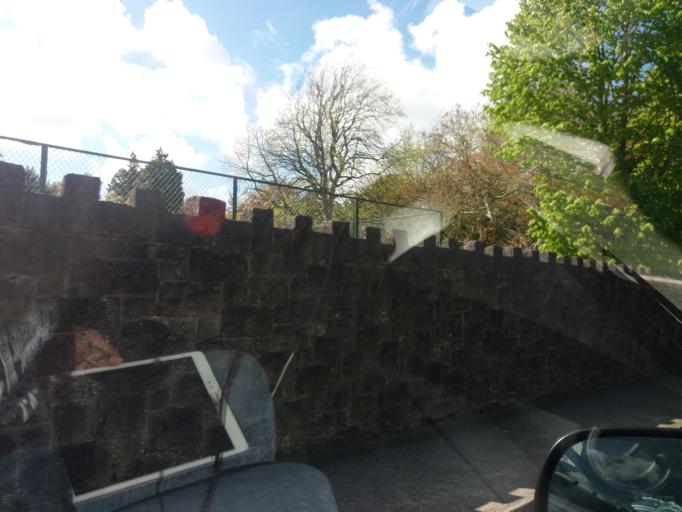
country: IE
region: Munster
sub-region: Waterford
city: Waterford
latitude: 52.2549
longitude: -7.1020
